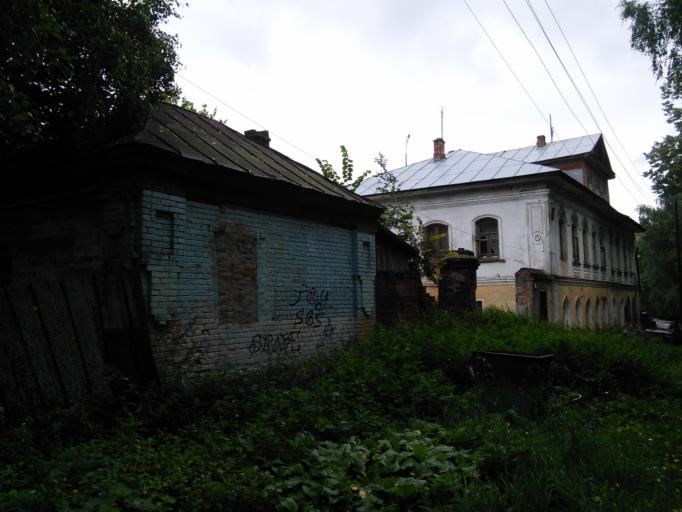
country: RU
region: Jaroslavl
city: Tutayev
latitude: 57.8798
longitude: 39.5384
